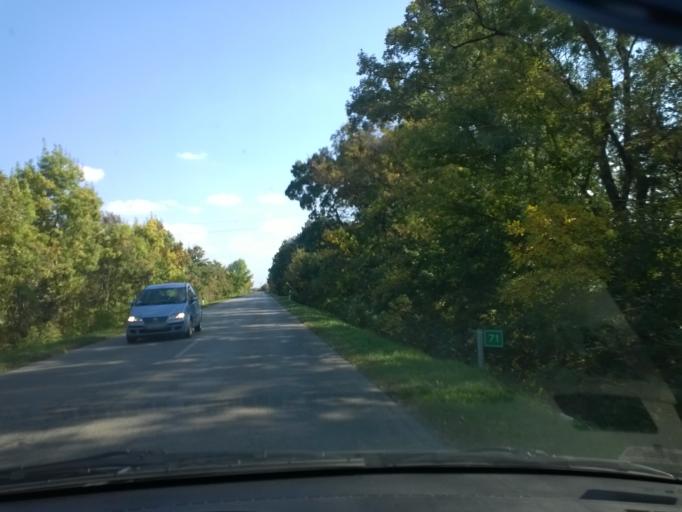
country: HU
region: Bacs-Kiskun
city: Kalocsa
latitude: 46.5138
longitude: 19.0051
